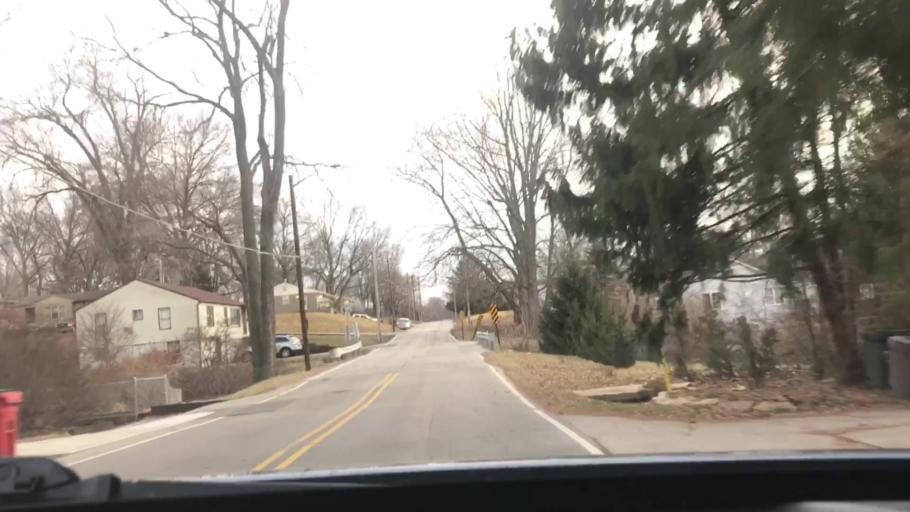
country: US
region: Missouri
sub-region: Jackson County
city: Independence
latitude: 39.0761
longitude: -94.4426
